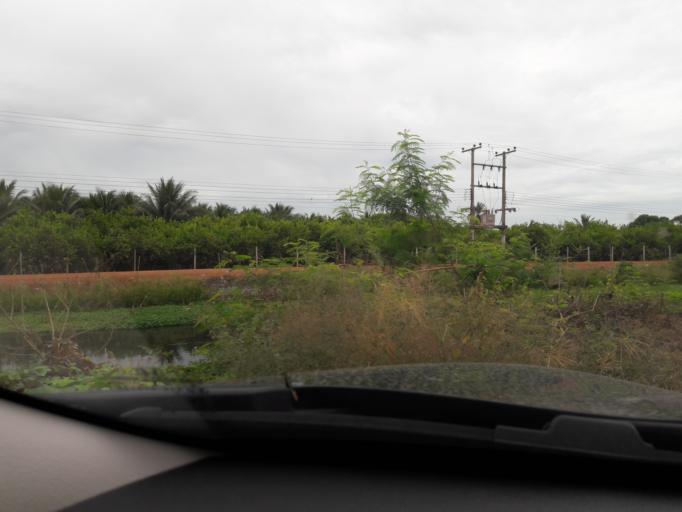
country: TH
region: Ratchaburi
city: Bang Phae
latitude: 13.6201
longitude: 99.9621
